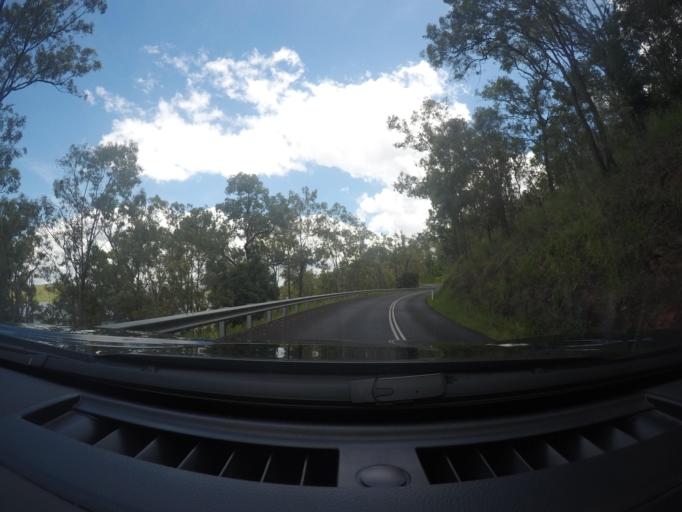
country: AU
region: Queensland
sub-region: Moreton Bay
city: Woodford
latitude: -27.0975
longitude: 152.5628
